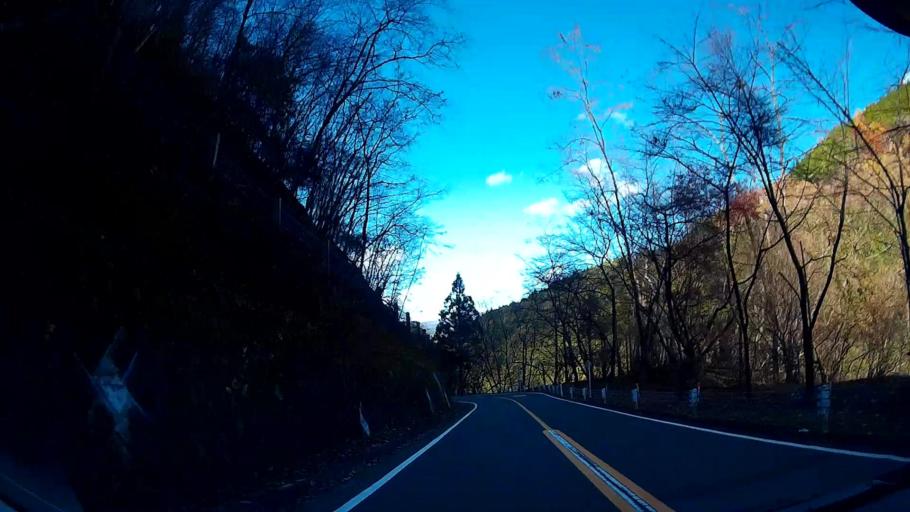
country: JP
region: Yamanashi
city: Uenohara
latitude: 35.7545
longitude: 139.0359
